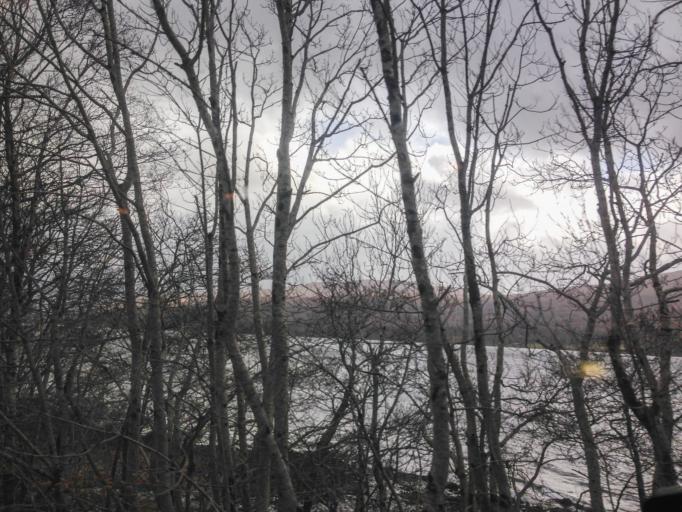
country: GB
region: Scotland
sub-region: Highland
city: Fort William
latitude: 56.8556
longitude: -5.2051
